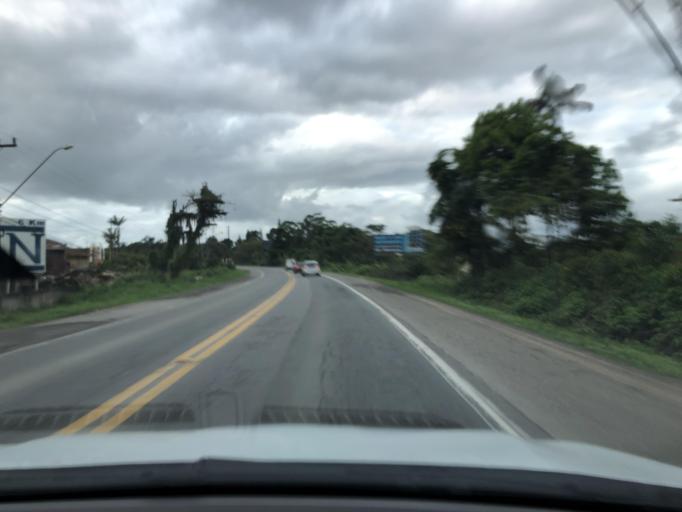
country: BR
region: Santa Catarina
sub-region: Sao Francisco Do Sul
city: Sao Francisco do Sul
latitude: -26.3032
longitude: -48.6403
